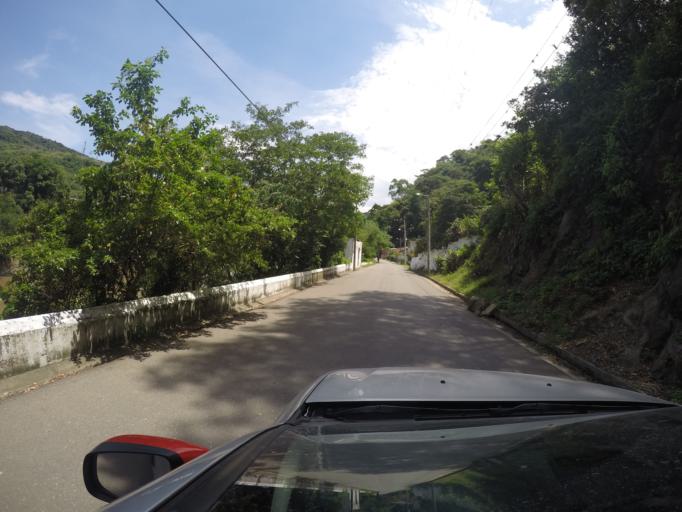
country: CO
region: Tolima
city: Honda
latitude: 5.2014
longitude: -74.7311
